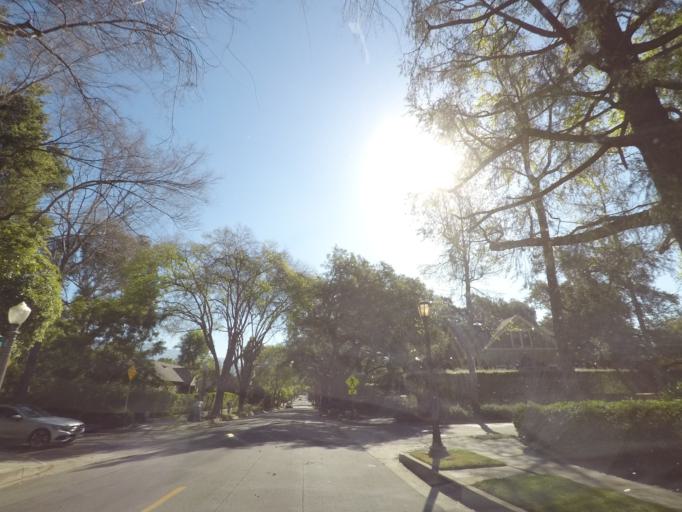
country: US
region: California
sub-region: Los Angeles County
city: La Canada Flintridge
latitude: 34.1714
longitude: -118.1797
